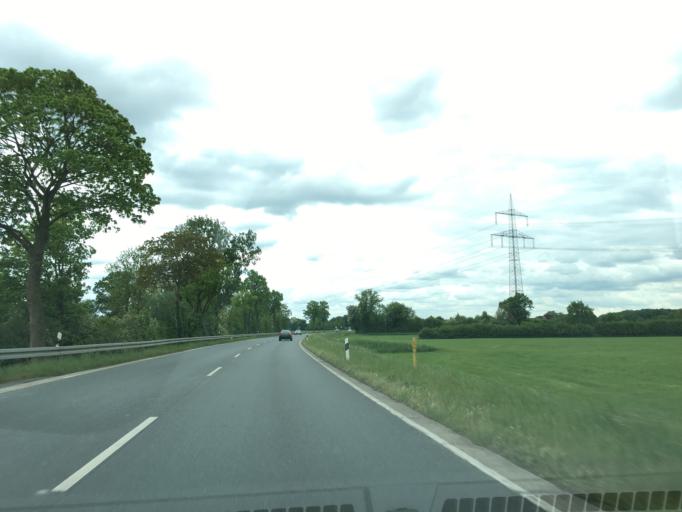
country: DE
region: North Rhine-Westphalia
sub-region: Regierungsbezirk Munster
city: Drensteinfurt
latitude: 51.8312
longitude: 7.6848
